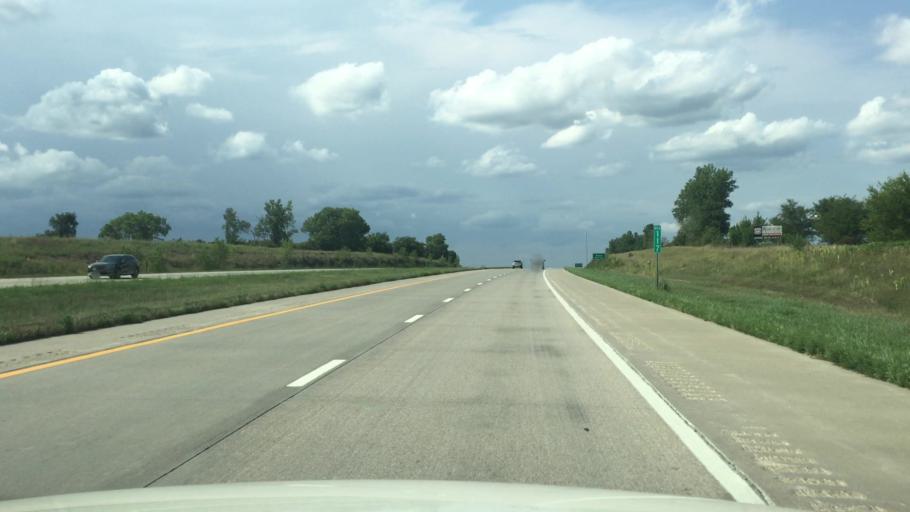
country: US
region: Kansas
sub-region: Miami County
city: Louisburg
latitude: 38.5544
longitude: -94.6904
